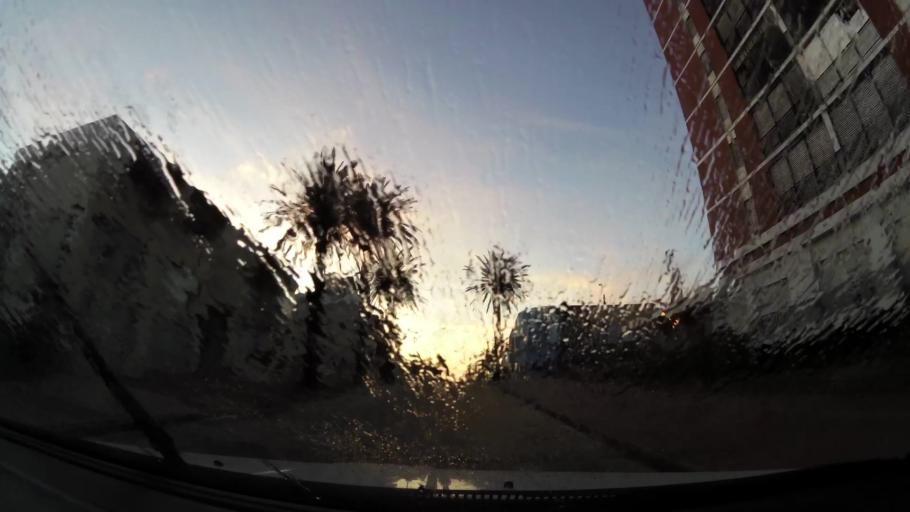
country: UY
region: Maldonado
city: Punta del Este
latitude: -34.9670
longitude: -54.9481
